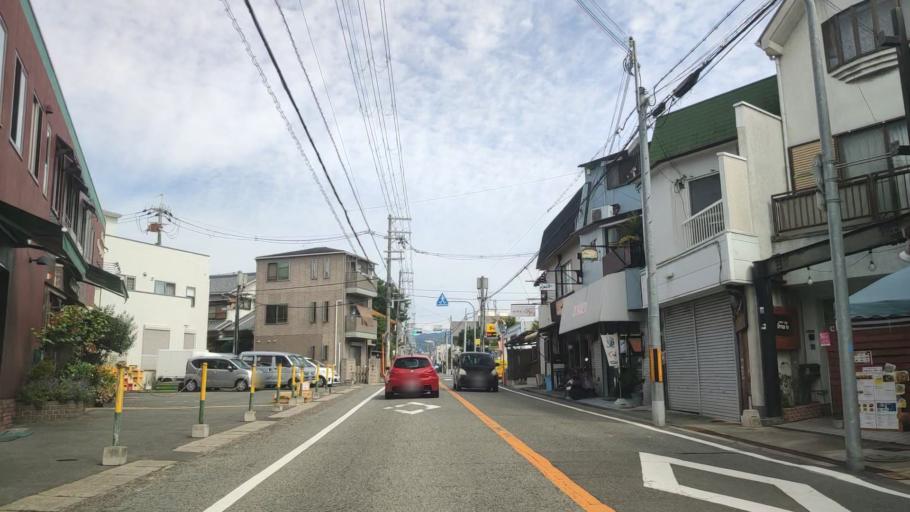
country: JP
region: Osaka
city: Mino
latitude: 34.8057
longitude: 135.4645
